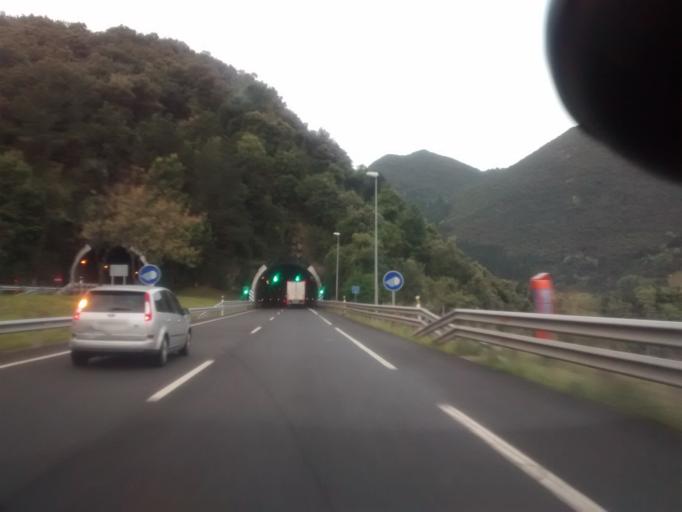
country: ES
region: Basque Country
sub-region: Provincia de Guipuzcoa
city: Deba
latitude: 43.2788
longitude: -2.3628
